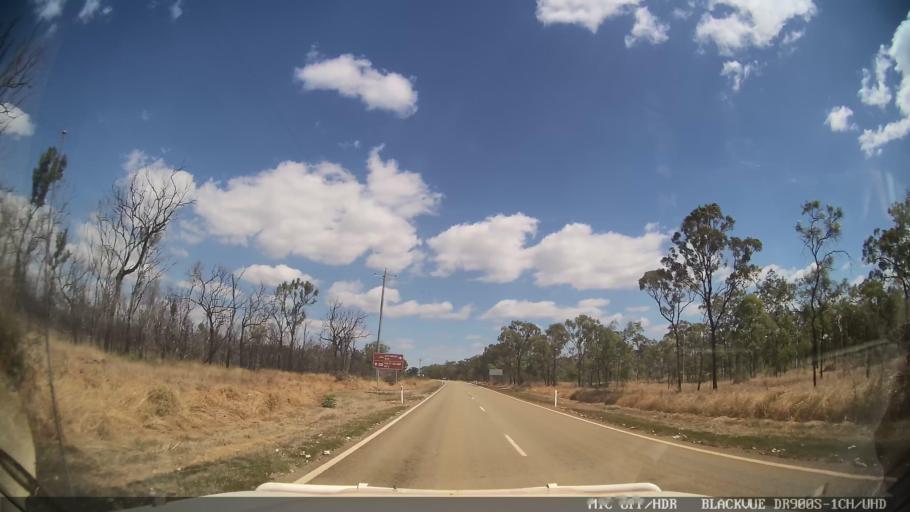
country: AU
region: Queensland
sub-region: Tablelands
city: Ravenshoe
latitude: -18.1331
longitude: 144.8143
